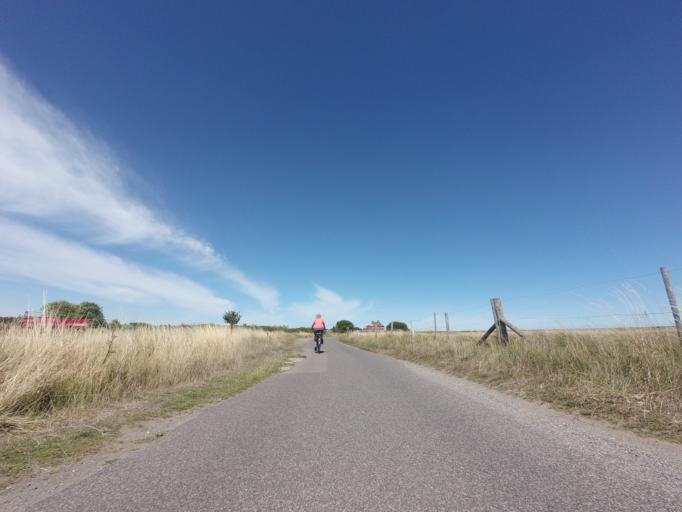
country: GB
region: England
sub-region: Kent
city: Deal
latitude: 51.2605
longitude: 1.3865
